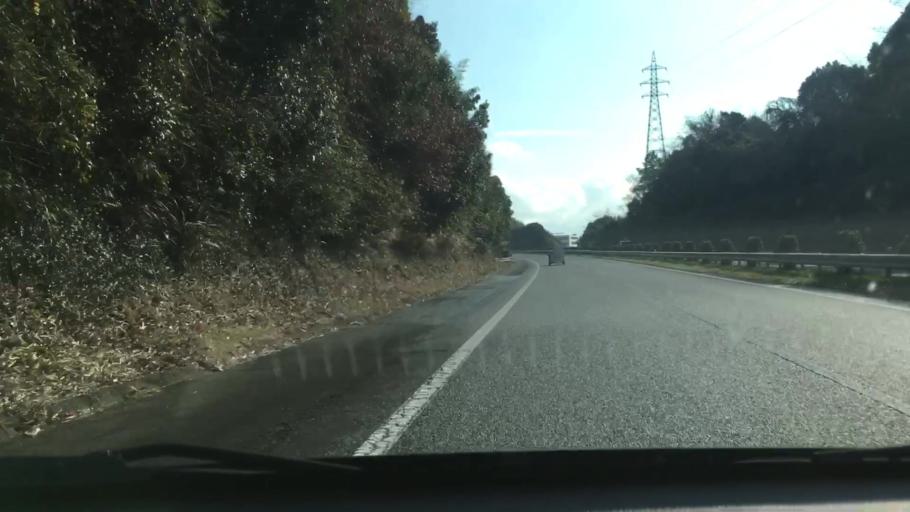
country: JP
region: Kumamoto
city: Matsubase
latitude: 32.6332
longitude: 130.7102
